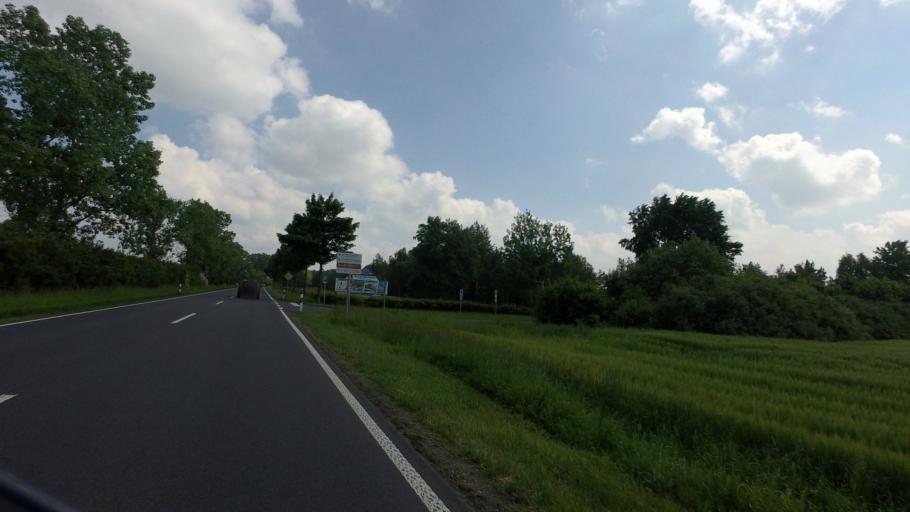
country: DE
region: Saxony
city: Trebendorf
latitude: 51.5481
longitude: 14.5586
